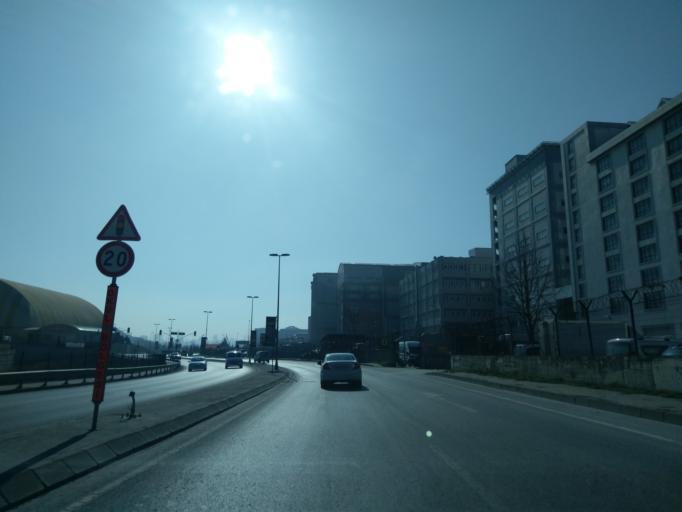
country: TR
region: Istanbul
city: Basaksehir
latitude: 41.0878
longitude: 28.8046
